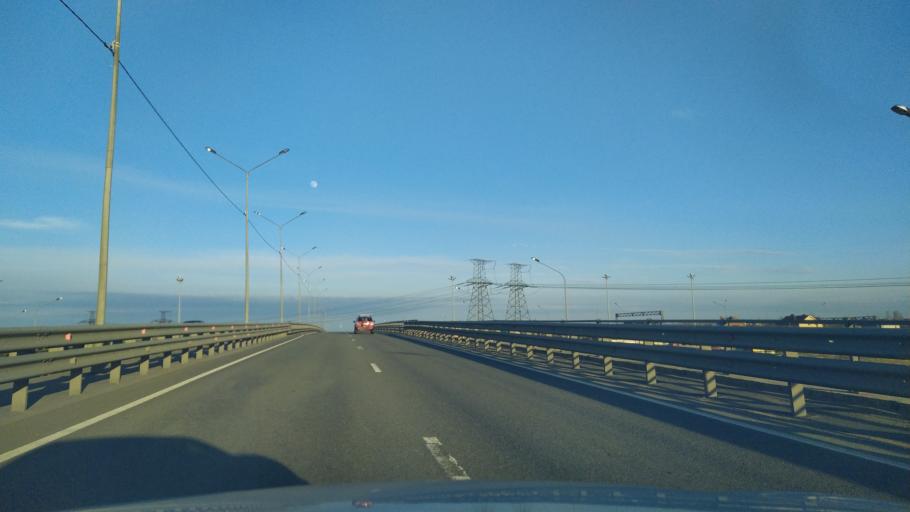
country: RU
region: St.-Petersburg
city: Aleksandrovskaya
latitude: 59.7454
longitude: 30.3070
